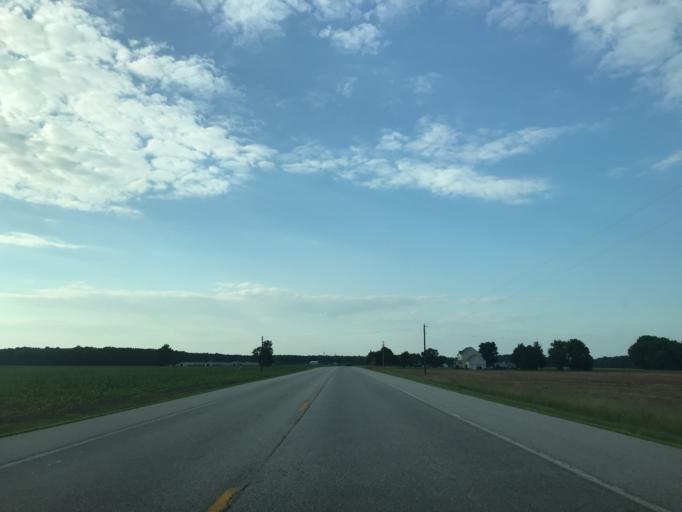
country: US
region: Maryland
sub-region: Caroline County
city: Federalsburg
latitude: 38.7760
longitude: -75.7873
